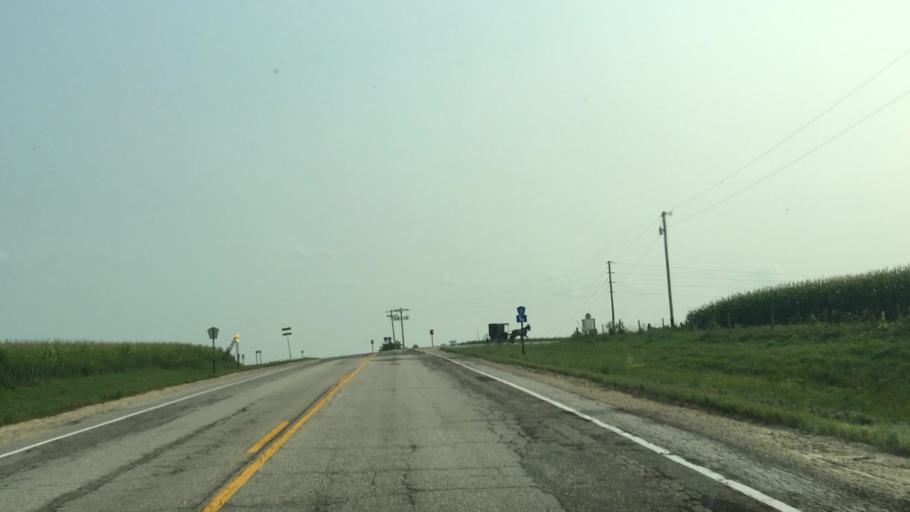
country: US
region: Minnesota
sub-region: Fillmore County
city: Harmony
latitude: 43.6528
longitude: -91.9301
